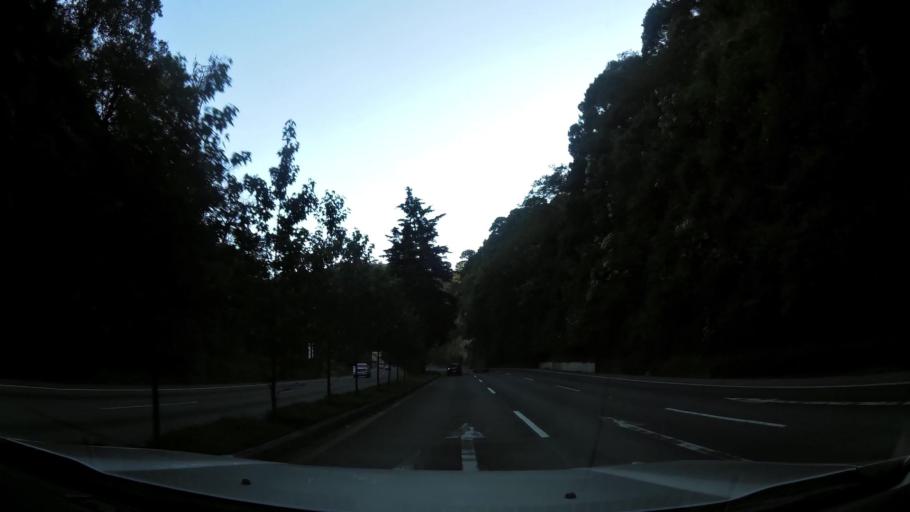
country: GT
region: Sacatepequez
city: San Lucas Sacatepequez
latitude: 14.6063
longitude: -90.6344
